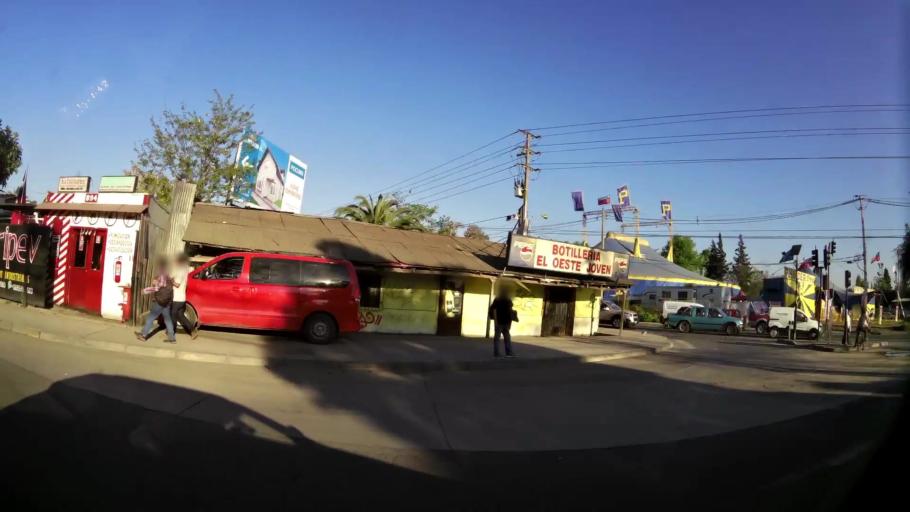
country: CL
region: Santiago Metropolitan
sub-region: Provincia de Talagante
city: Penaflor
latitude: -33.6096
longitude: -70.8572
